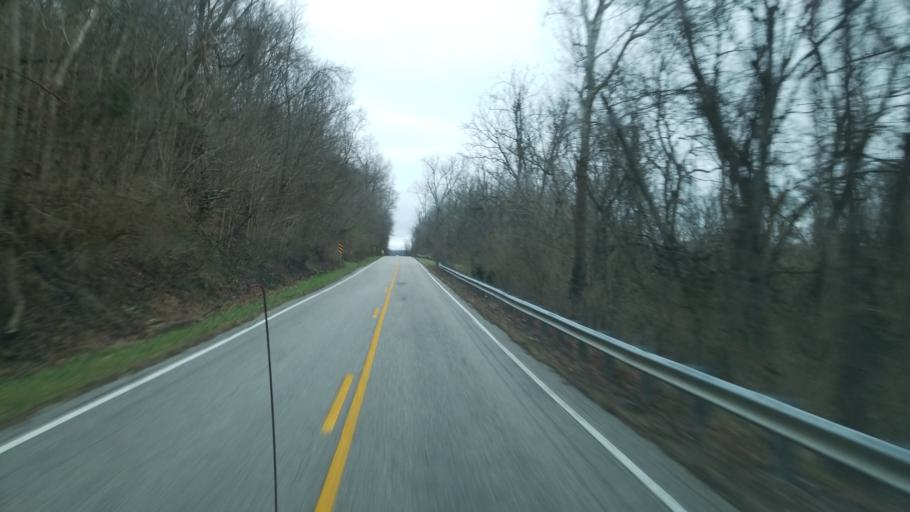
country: US
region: Kentucky
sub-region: Bracken County
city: Brooksville
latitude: 38.7806
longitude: -84.1337
